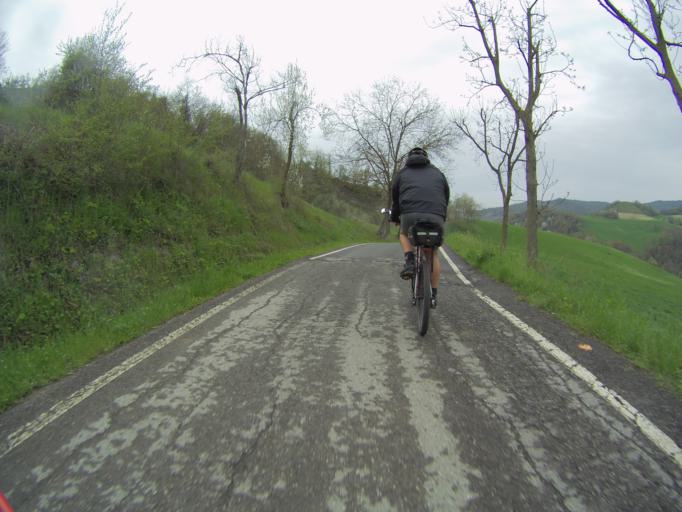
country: IT
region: Emilia-Romagna
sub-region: Provincia di Reggio Emilia
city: Quattro Castella
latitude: 44.6181
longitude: 10.4894
